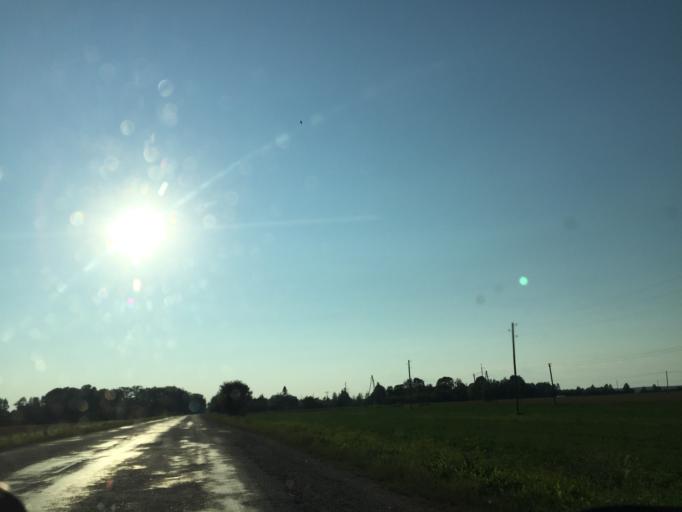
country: LV
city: Tervete
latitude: 56.4408
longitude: 23.4875
